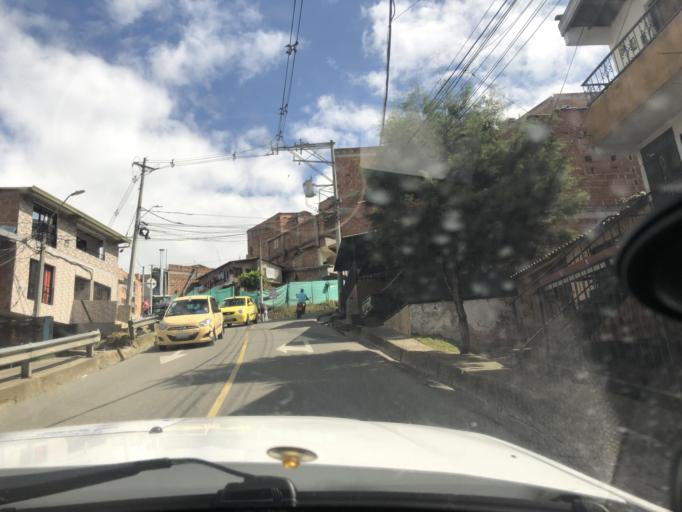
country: CO
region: Antioquia
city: Bello
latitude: 6.3091
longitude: -75.5492
